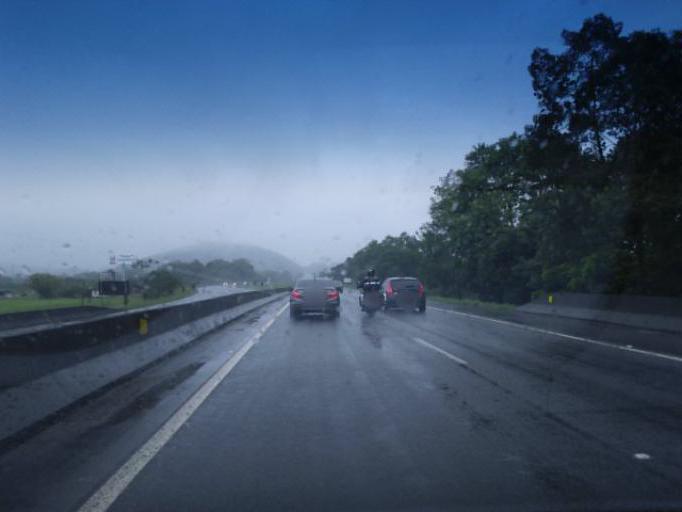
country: BR
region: Santa Catarina
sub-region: Joinville
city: Joinville
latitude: -26.1082
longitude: -48.8730
